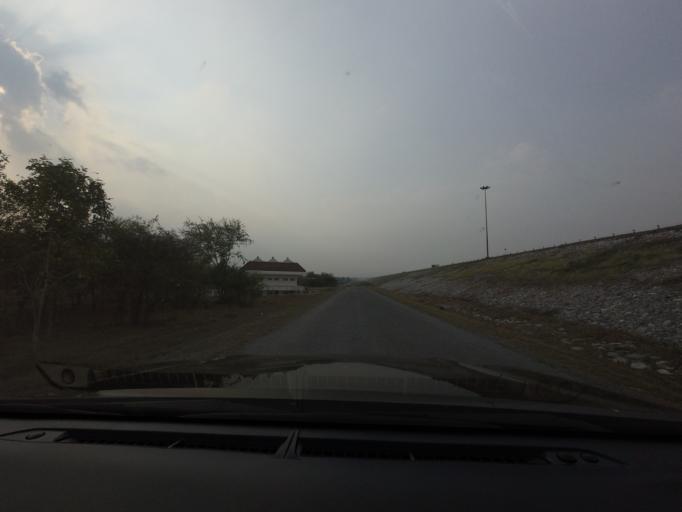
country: TH
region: Sara Buri
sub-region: Amphoe Wang Muang
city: Wang Muang
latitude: 14.8459
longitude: 101.0928
